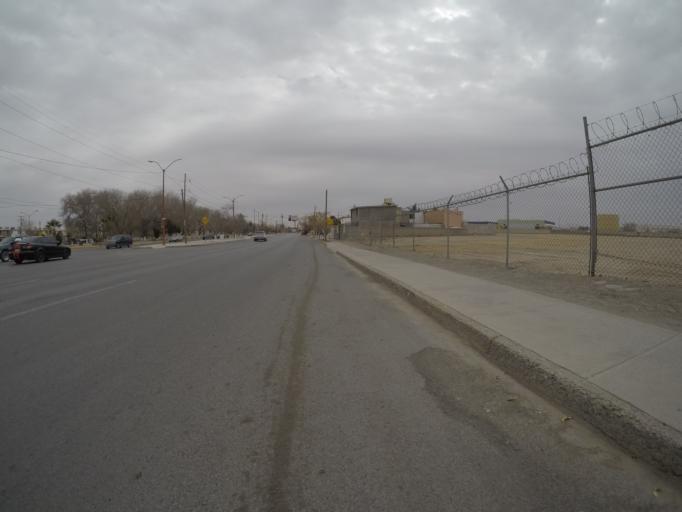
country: MX
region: Chihuahua
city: Ciudad Juarez
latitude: 31.7380
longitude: -106.4201
